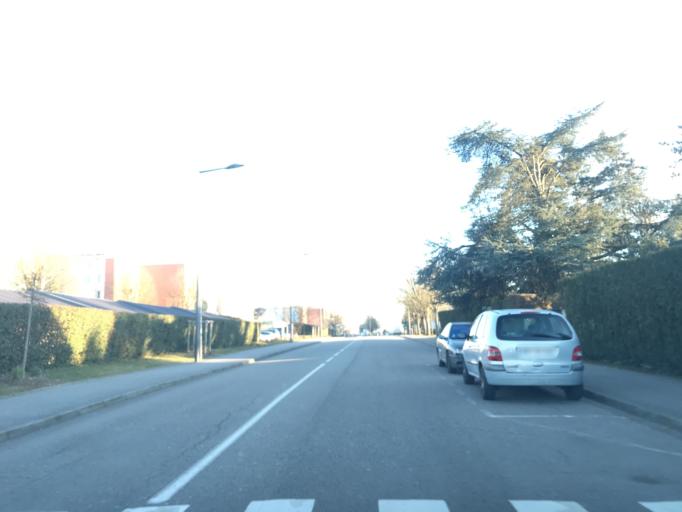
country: FR
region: Haute-Normandie
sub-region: Departement de l'Eure
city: Evreux
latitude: 49.0131
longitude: 1.1643
